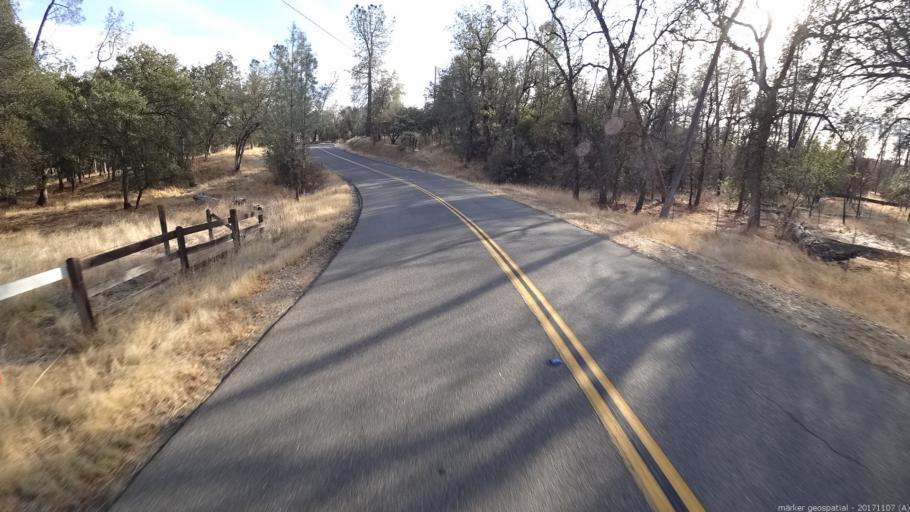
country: US
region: California
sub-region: Shasta County
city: Redding
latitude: 40.5060
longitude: -122.4472
